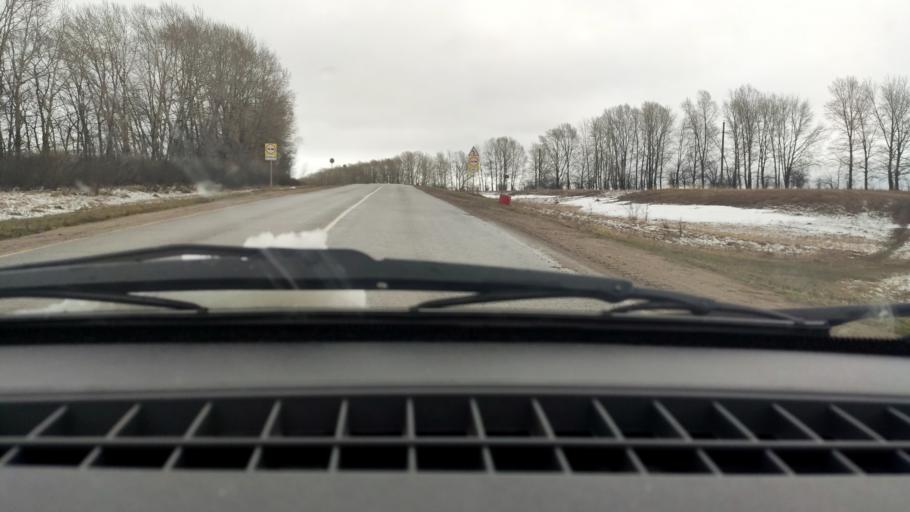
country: RU
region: Bashkortostan
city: Alekseyevka
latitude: 55.0660
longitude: 55.0950
